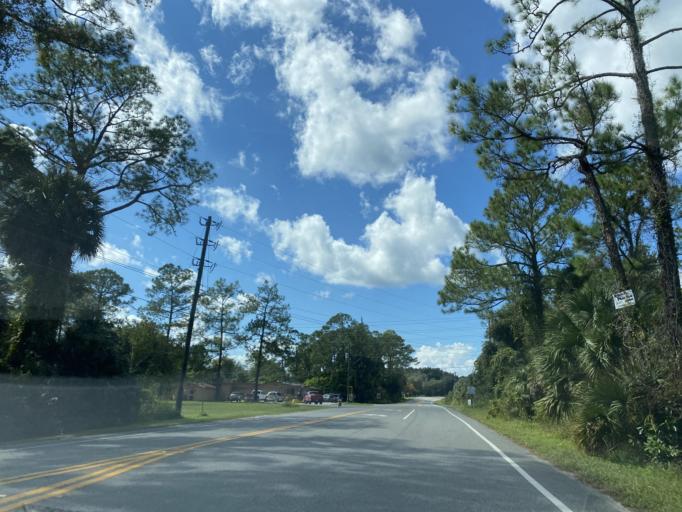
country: US
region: Florida
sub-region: Lake County
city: Lake Mack-Forest Hills
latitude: 29.0042
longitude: -81.4324
